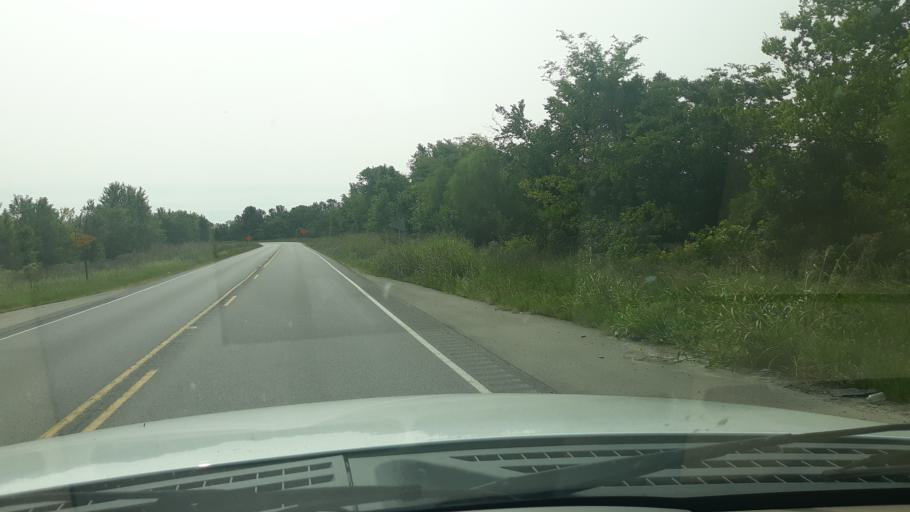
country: US
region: Illinois
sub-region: Wabash County
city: Mount Carmel
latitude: 38.3597
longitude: -87.6937
